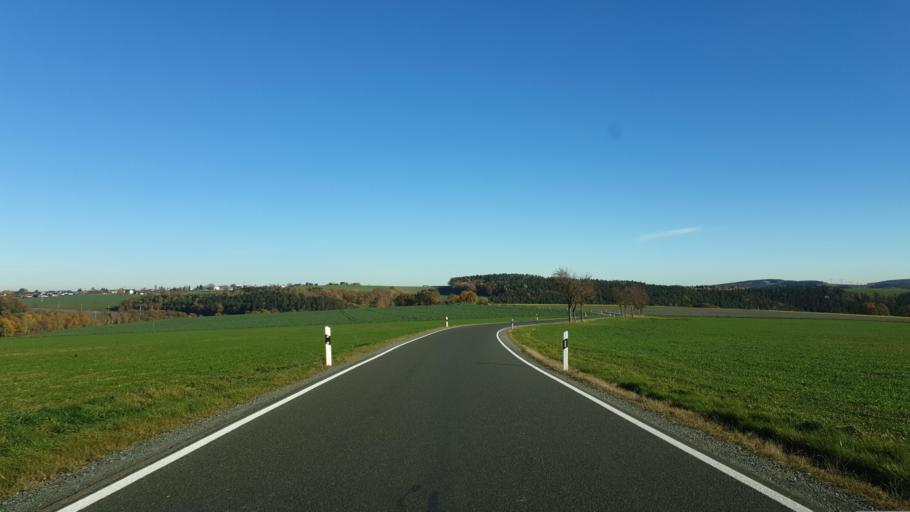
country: DE
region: Saxony
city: Elsterberg
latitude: 50.6276
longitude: 12.1276
